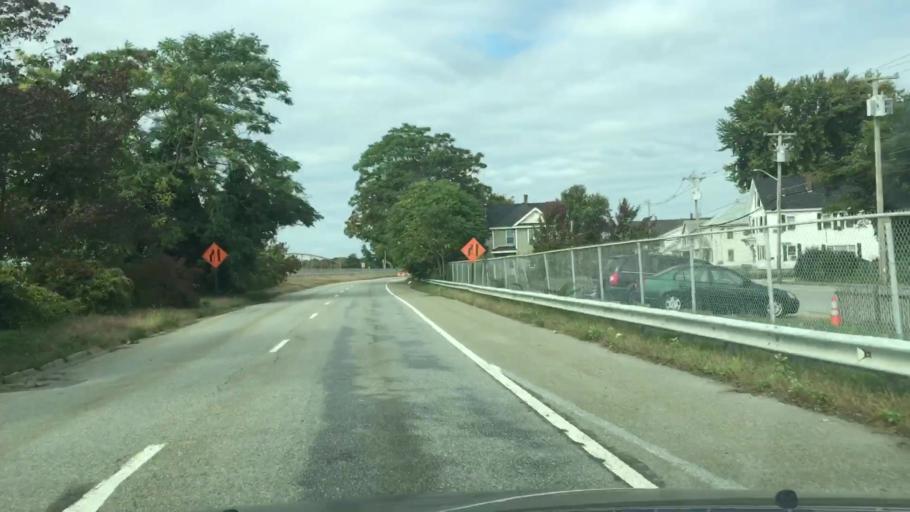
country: US
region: Massachusetts
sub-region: Middlesex County
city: Dracut
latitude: 42.6530
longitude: -71.3107
